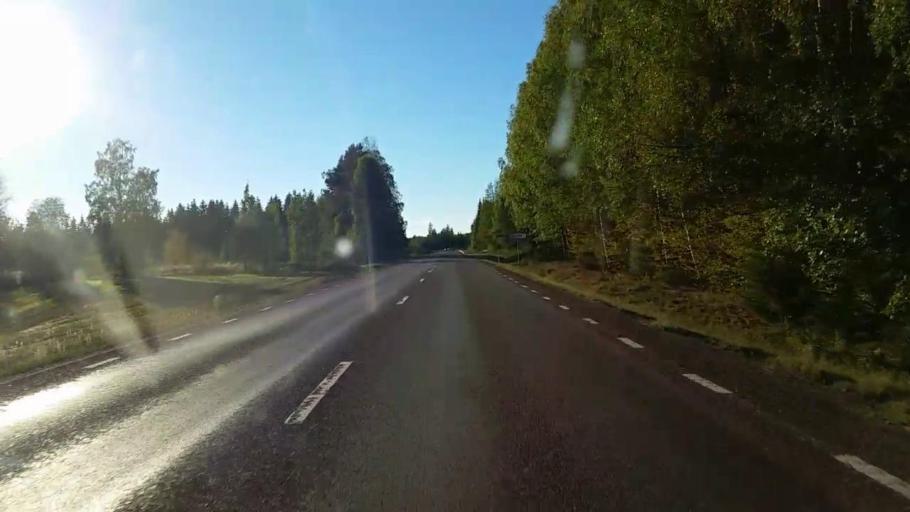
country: SE
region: Gaevleborg
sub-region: Ljusdals Kommun
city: Ljusdal
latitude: 61.8188
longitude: 16.1765
